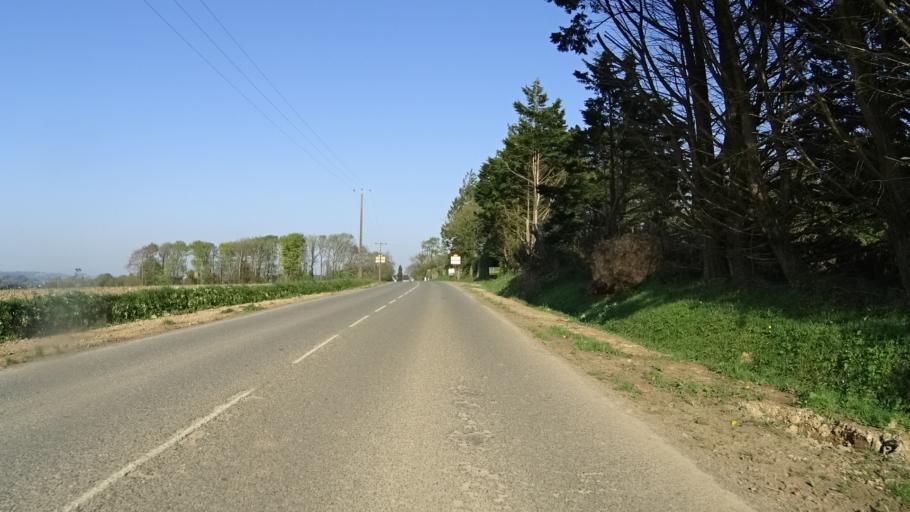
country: FR
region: Brittany
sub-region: Departement du Finistere
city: Irvillac
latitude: 48.3688
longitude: -4.2203
